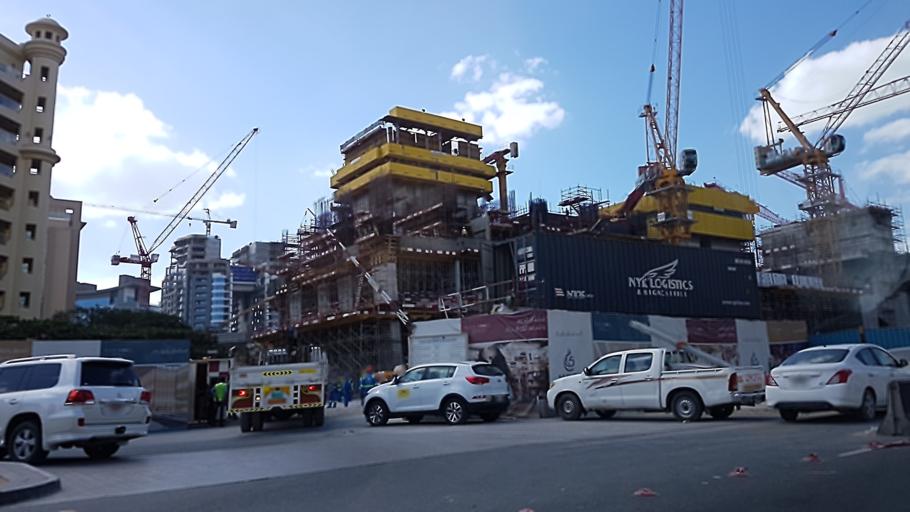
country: AE
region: Dubai
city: Dubai
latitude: 25.1138
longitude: 55.1410
